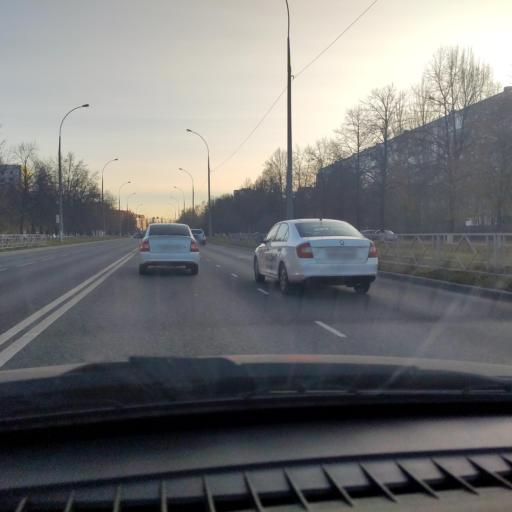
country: RU
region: Samara
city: Tol'yatti
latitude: 53.5216
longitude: 49.3106
